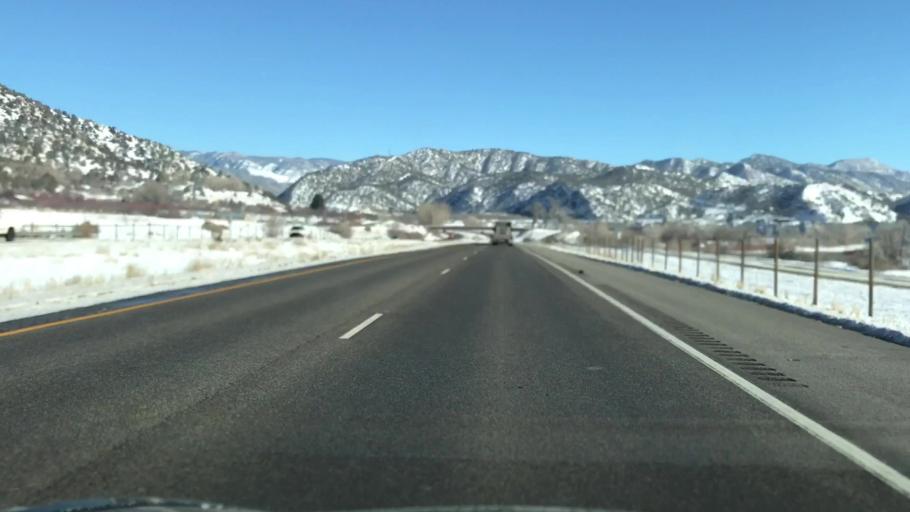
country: US
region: Colorado
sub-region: Garfield County
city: New Castle
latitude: 39.5558
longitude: -107.5683
